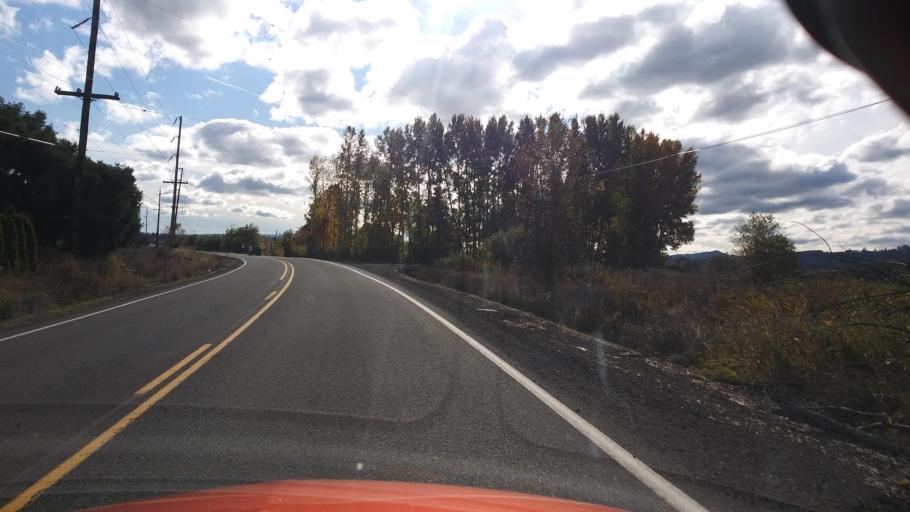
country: US
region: Oregon
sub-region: Washington County
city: Banks
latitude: 45.5832
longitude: -123.1143
